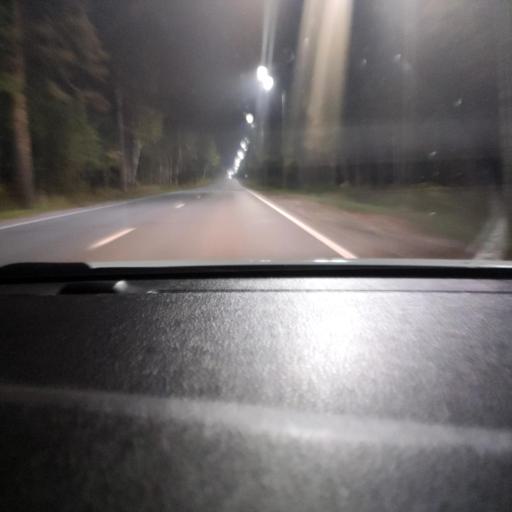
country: RU
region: Tatarstan
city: Stolbishchi
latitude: 55.6360
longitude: 49.0681
